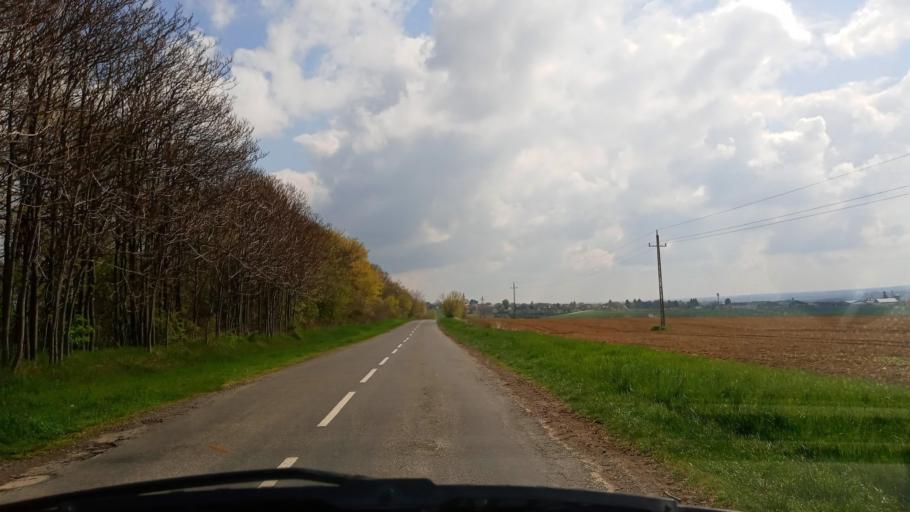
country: HU
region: Baranya
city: Pecsvarad
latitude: 46.1080
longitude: 18.5016
